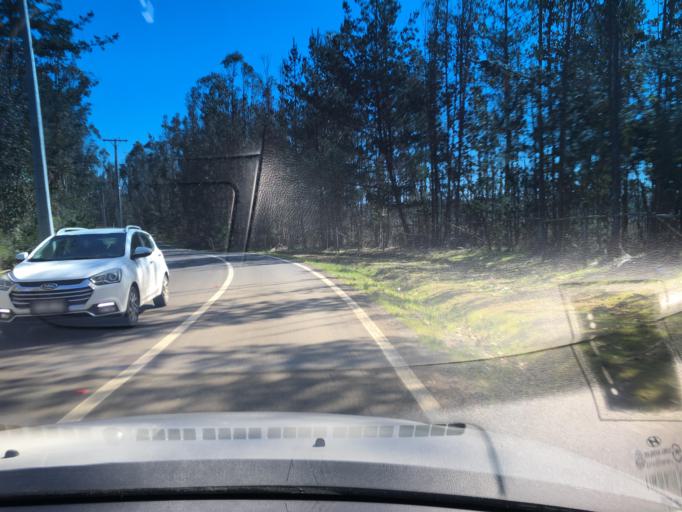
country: CL
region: Valparaiso
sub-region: San Antonio Province
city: El Tabo
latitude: -33.4099
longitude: -71.6023
